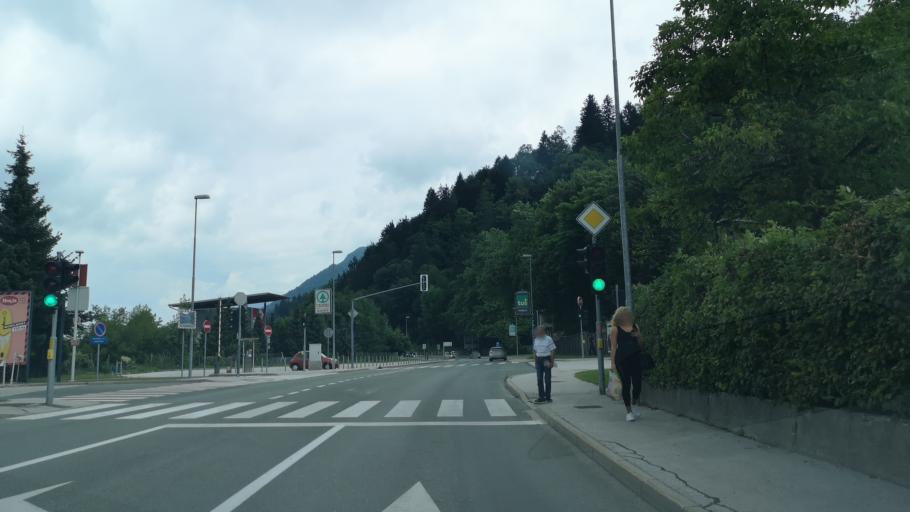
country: SI
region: Jesenice
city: Hrusica
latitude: 46.4421
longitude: 14.0367
